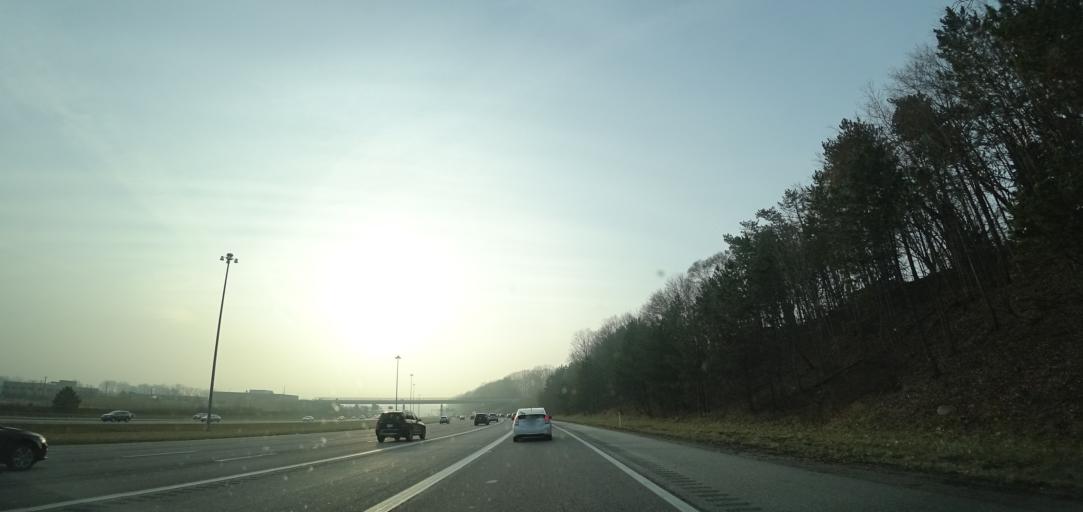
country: US
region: Ohio
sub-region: Cuyahoga County
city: Seven Hills
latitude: 41.4115
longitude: -81.6706
